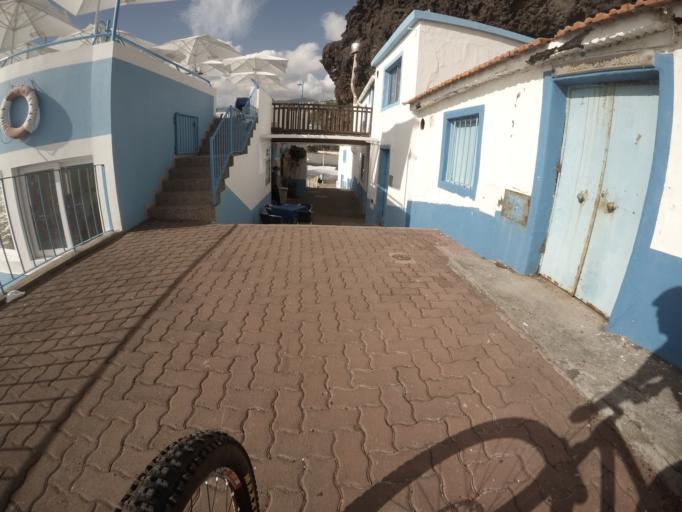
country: PT
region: Madeira
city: Camara de Lobos
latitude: 32.6354
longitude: -16.9477
